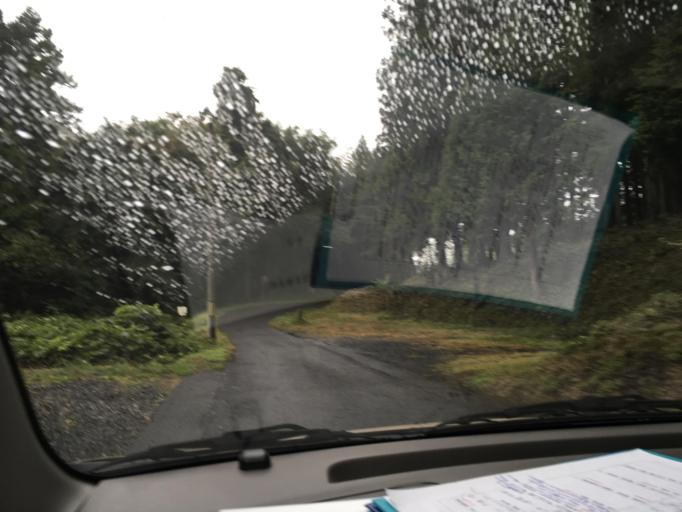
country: JP
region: Iwate
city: Ichinoseki
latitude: 38.8168
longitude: 141.1917
